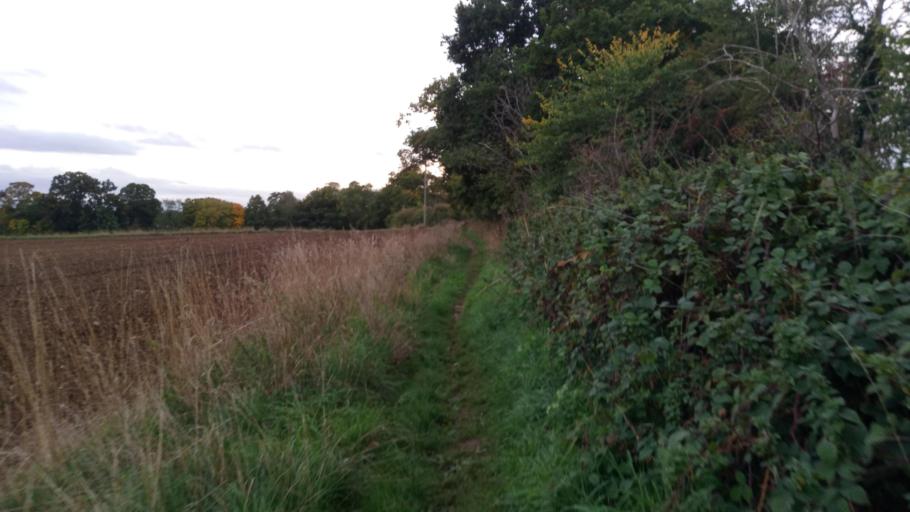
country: GB
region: England
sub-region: Cambridgeshire
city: Linton
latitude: 52.0534
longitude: 0.3059
